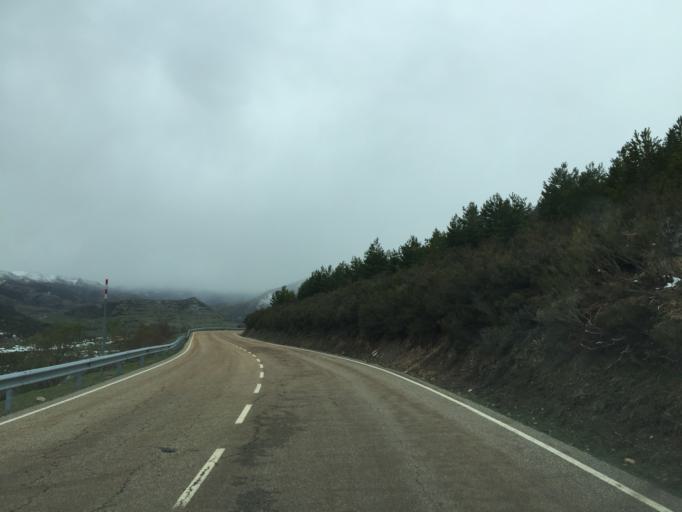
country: ES
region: Castille and Leon
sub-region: Provincia de Leon
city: San Emiliano
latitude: 43.0426
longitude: -6.0125
